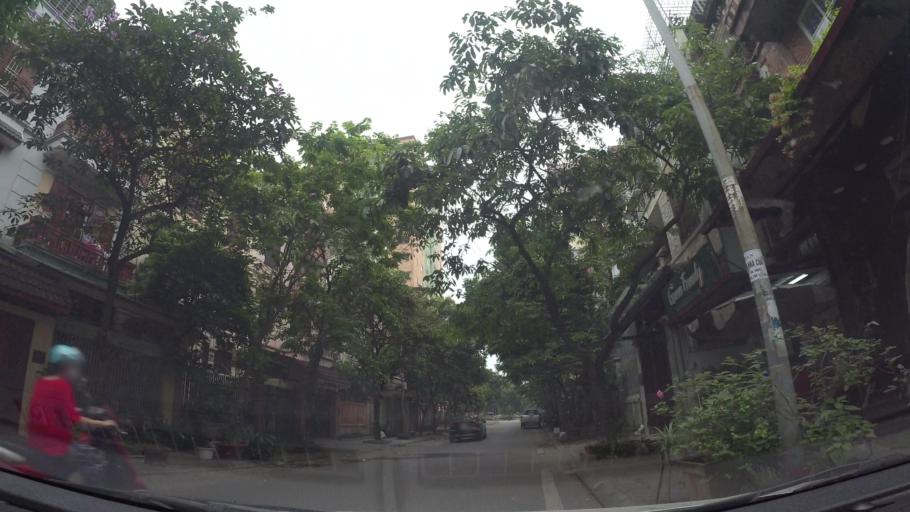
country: VN
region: Ha Noi
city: Cau Dien
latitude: 21.0309
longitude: 105.7635
